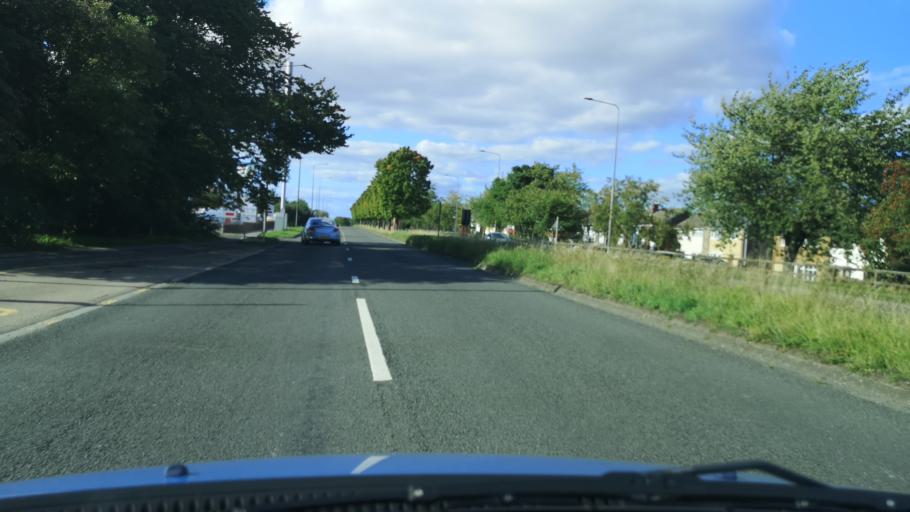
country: GB
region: England
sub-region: Doncaster
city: Carcroft
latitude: 53.5681
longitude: -1.1984
